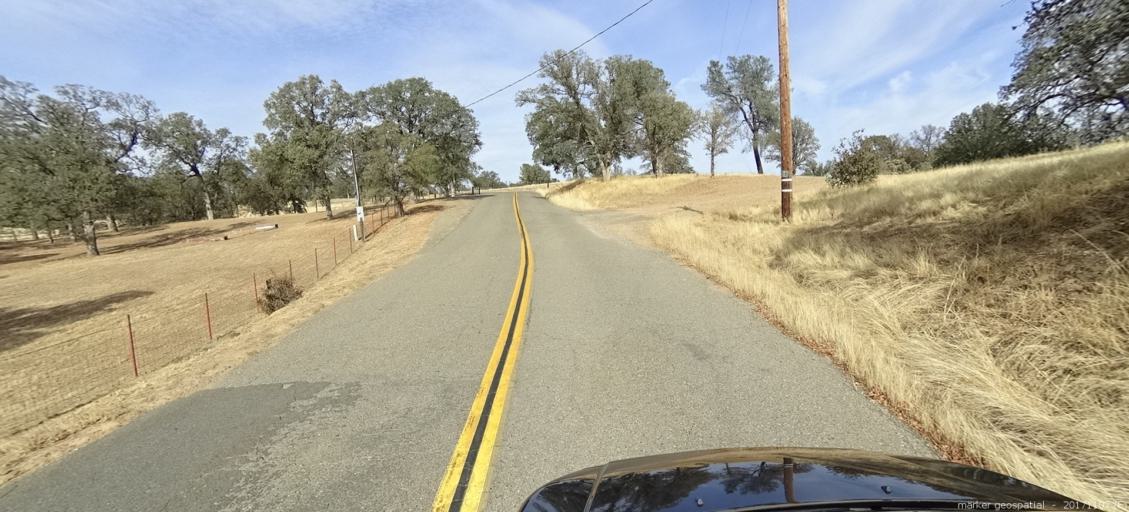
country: US
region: California
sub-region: Shasta County
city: Shasta
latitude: 40.4308
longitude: -122.5211
